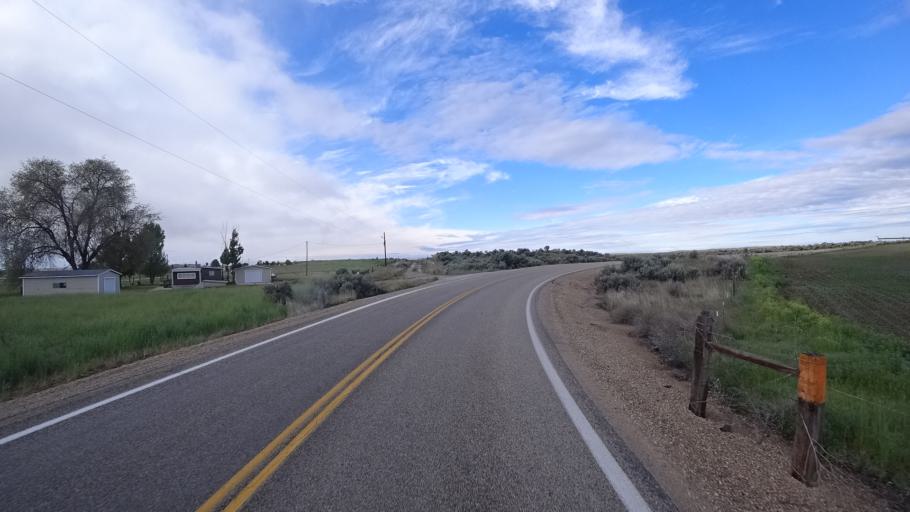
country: US
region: Idaho
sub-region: Ada County
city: Star
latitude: 43.7727
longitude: -116.4731
